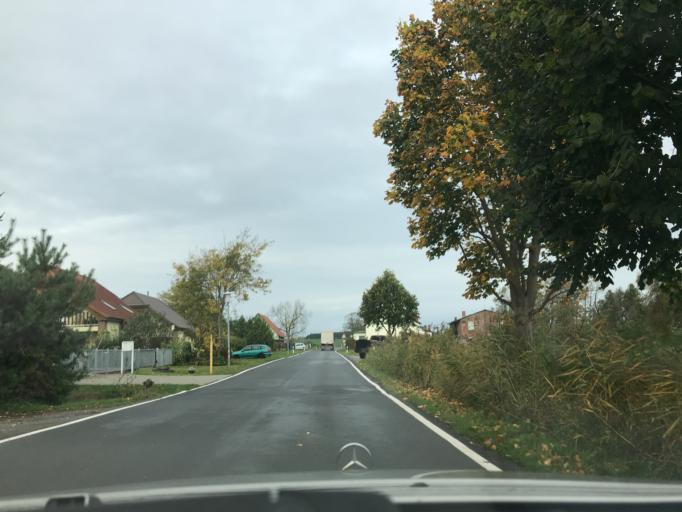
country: DE
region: Mecklenburg-Vorpommern
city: Kroslin
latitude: 54.1225
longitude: 13.7466
